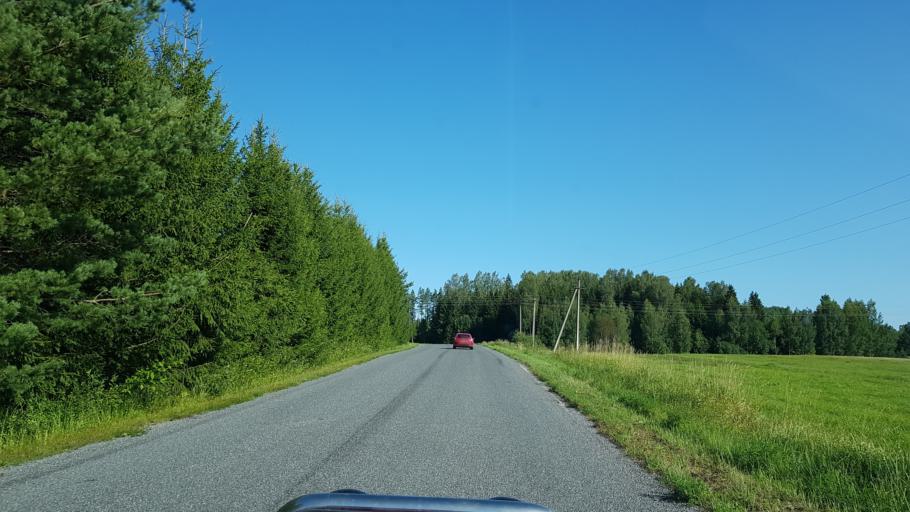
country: EE
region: Vorumaa
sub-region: Voru linn
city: Voru
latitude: 57.7348
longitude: 26.9275
